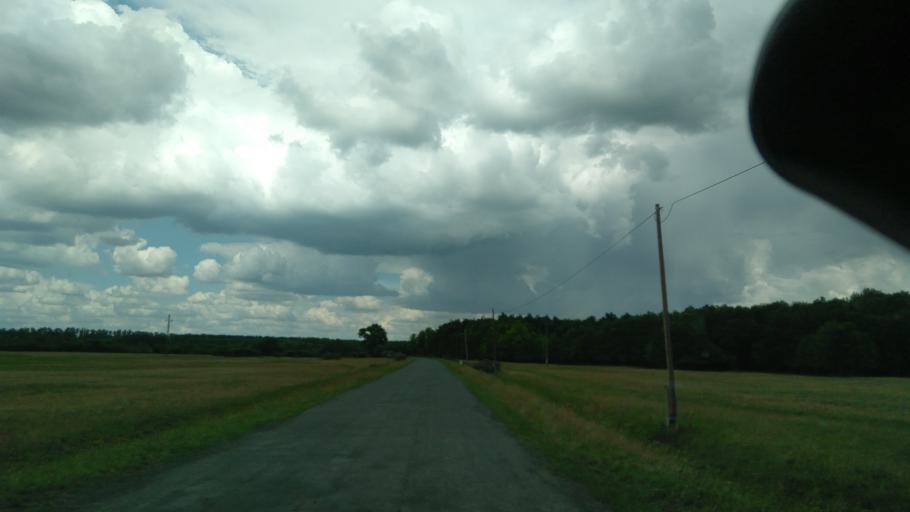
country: HU
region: Bekes
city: Szeghalom
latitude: 47.1069
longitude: 21.0845
